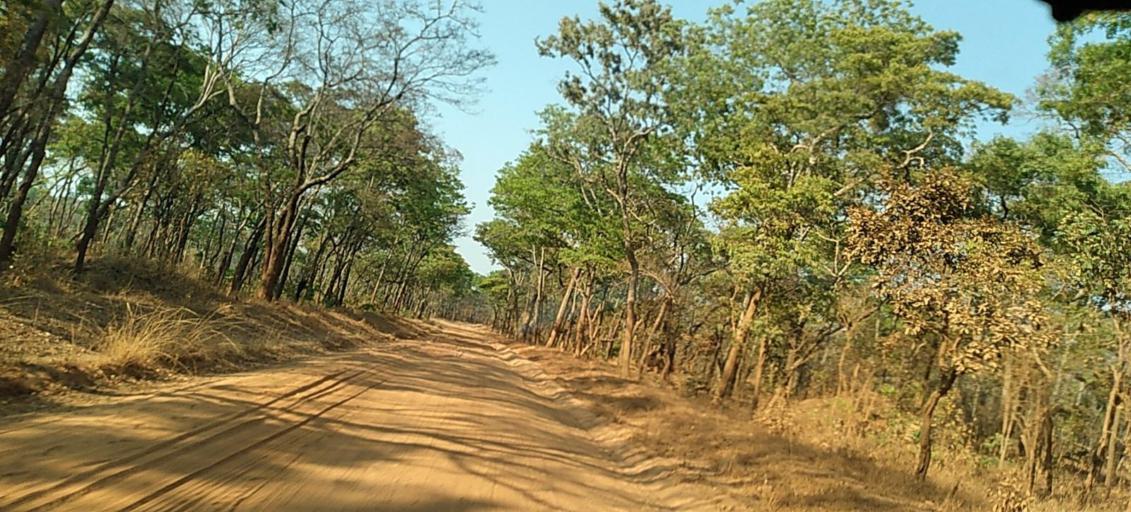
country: ZM
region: North-Western
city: Kasempa
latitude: -13.5785
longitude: 25.9903
